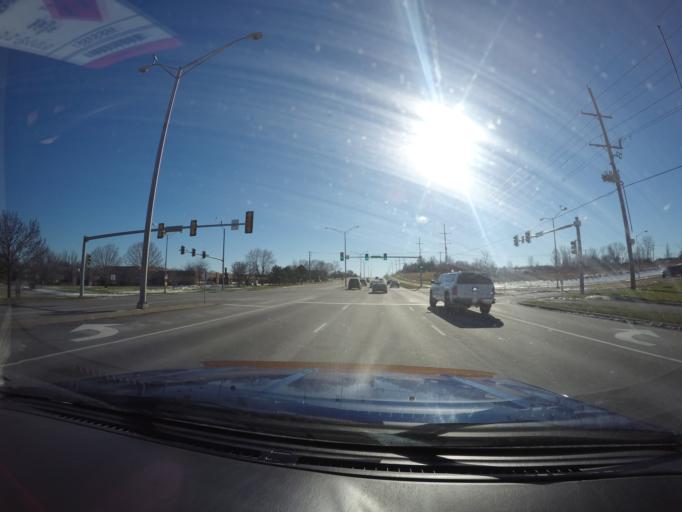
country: US
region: Kansas
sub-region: Johnson County
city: Leawood
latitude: 38.9255
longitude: -94.6490
